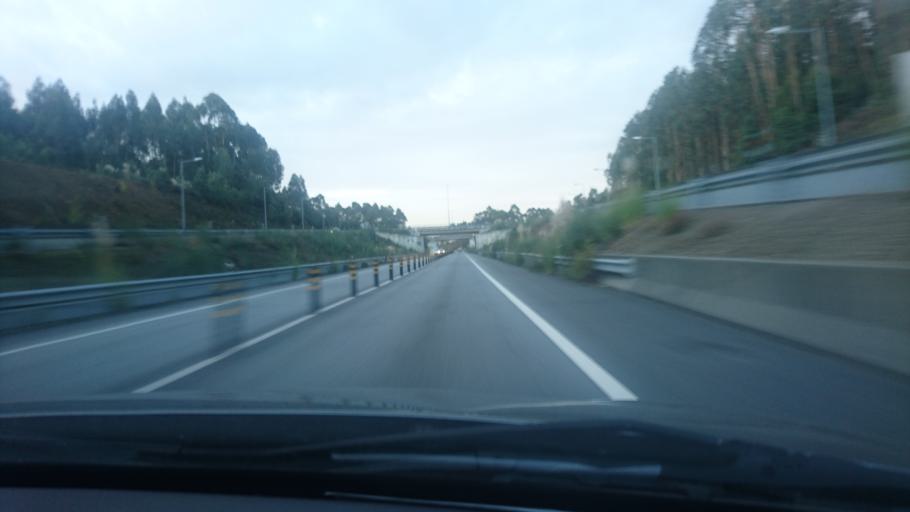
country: PT
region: Aveiro
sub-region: Santa Maria da Feira
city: Arrifana
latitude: 40.9260
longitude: -8.4864
